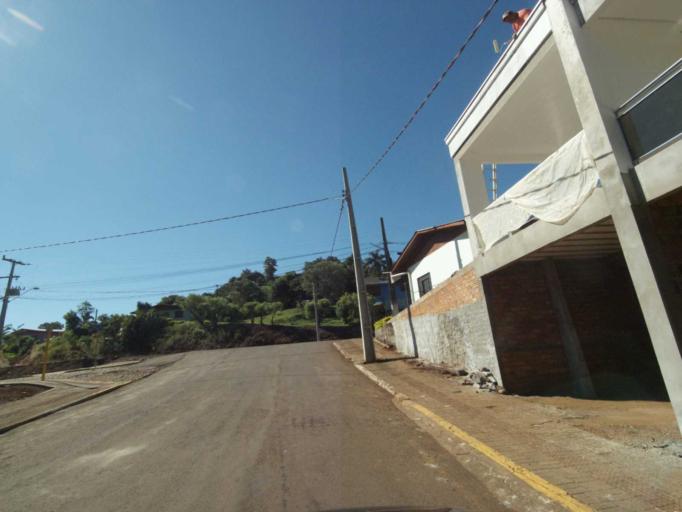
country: BR
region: Parana
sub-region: Francisco Beltrao
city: Francisco Beltrao
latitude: -26.1430
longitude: -53.3101
